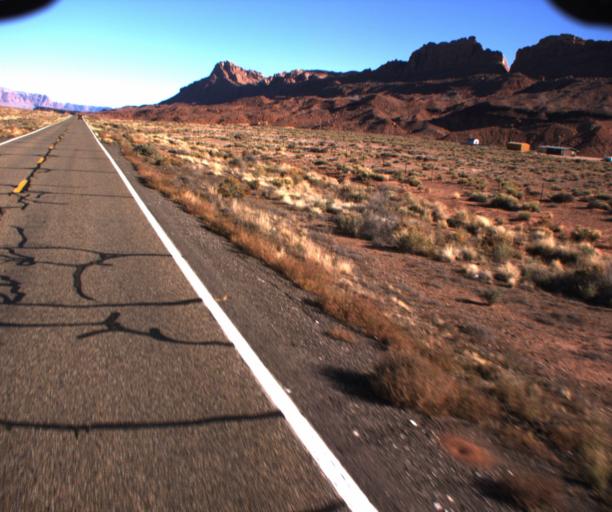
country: US
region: Arizona
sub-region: Coconino County
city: LeChee
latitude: 36.6499
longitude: -111.6511
